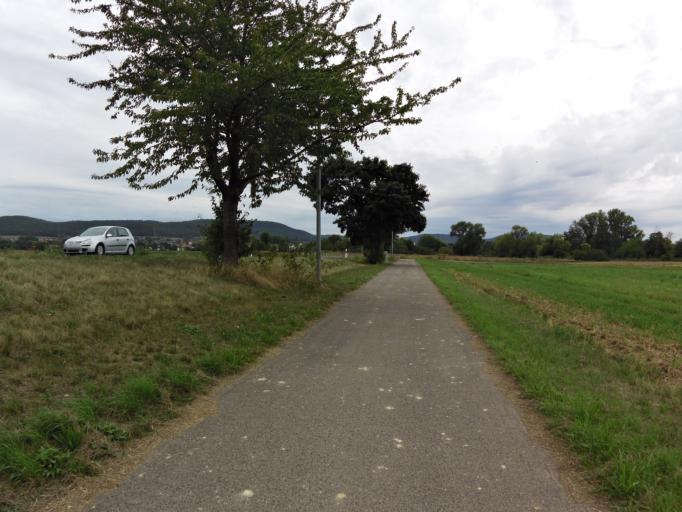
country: DE
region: Bavaria
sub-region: Regierungsbezirk Unterfranken
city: Zeil
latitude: 49.9998
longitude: 10.5903
